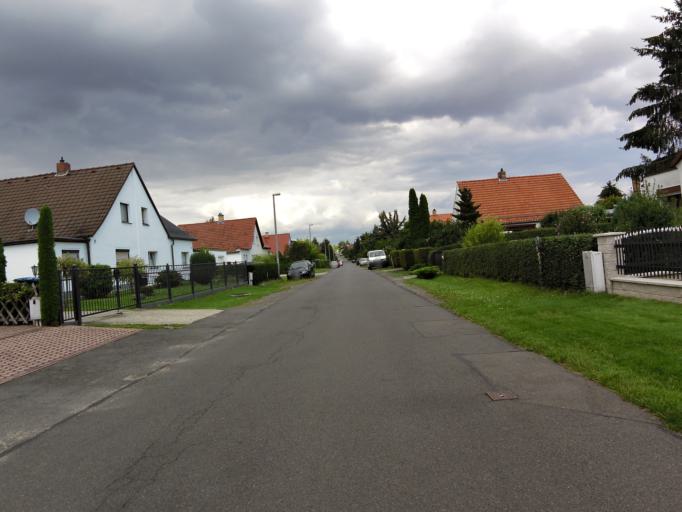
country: DE
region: Saxony
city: Leipzig
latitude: 51.3804
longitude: 12.4085
